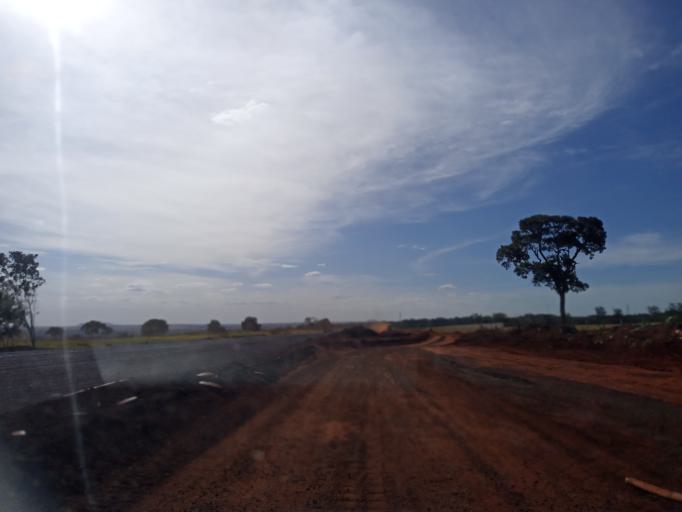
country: BR
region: Minas Gerais
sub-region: Ituiutaba
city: Ituiutaba
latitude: -18.9718
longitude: -49.5053
